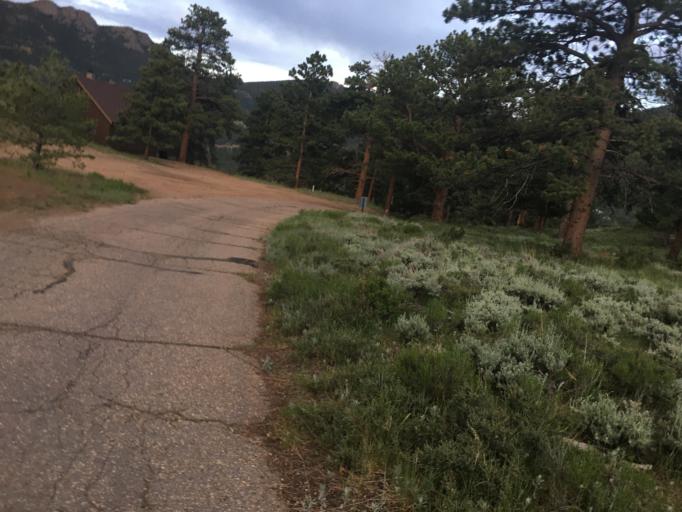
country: US
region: Colorado
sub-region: Larimer County
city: Estes Park
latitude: 40.3380
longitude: -105.5833
